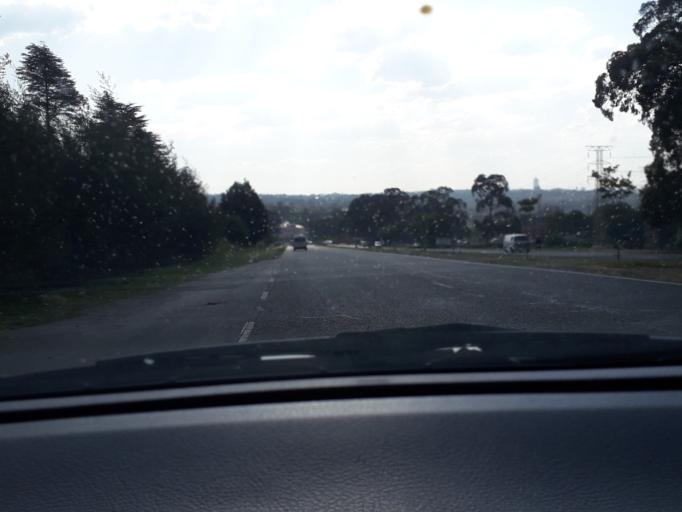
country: ZA
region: Gauteng
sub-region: City of Johannesburg Metropolitan Municipality
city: Modderfontein
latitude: -26.1277
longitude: 28.1279
